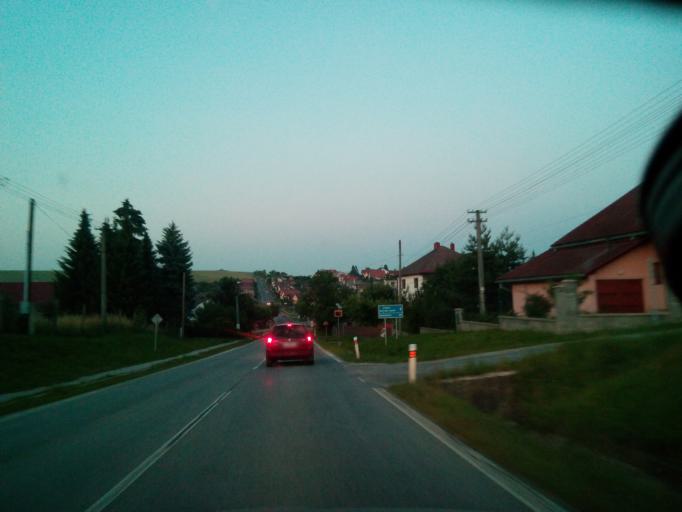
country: SK
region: Kosicky
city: Spisska Nova Ves
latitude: 48.9335
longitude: 20.6296
